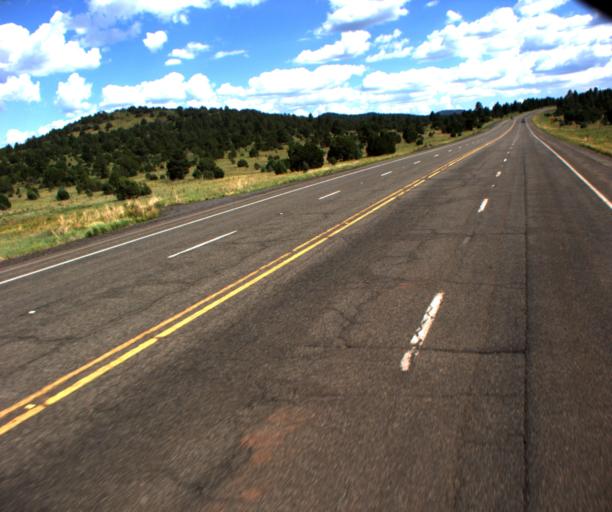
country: US
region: Arizona
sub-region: Coconino County
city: Williams
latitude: 35.3042
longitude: -112.1440
